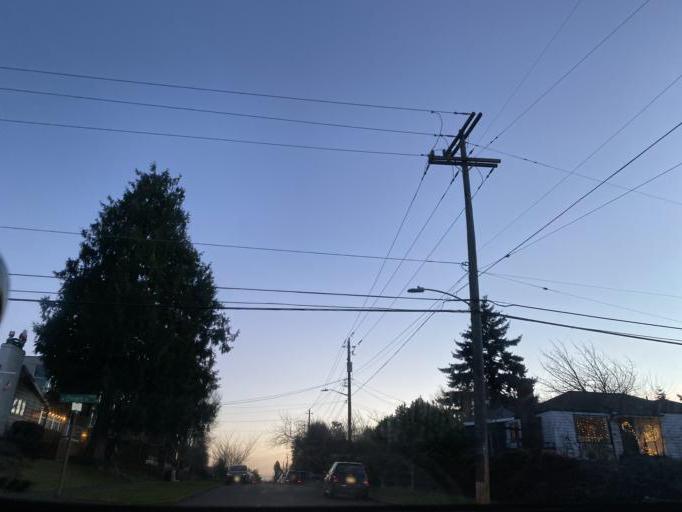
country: US
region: Washington
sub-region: King County
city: Seattle
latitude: 47.6578
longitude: -122.3995
